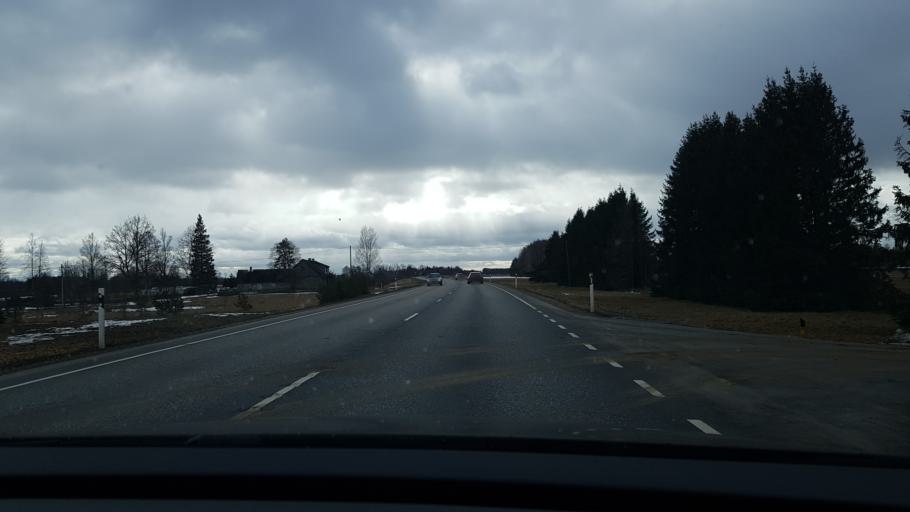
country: EE
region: Paernumaa
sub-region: Tootsi vald
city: Tootsi
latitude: 58.6071
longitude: 24.9154
